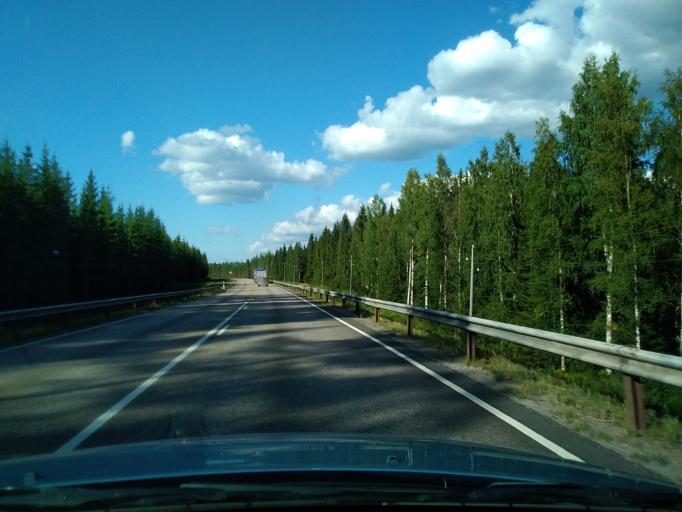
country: FI
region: Pirkanmaa
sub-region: Ylae-Pirkanmaa
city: Maenttae
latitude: 62.0851
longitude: 24.7276
